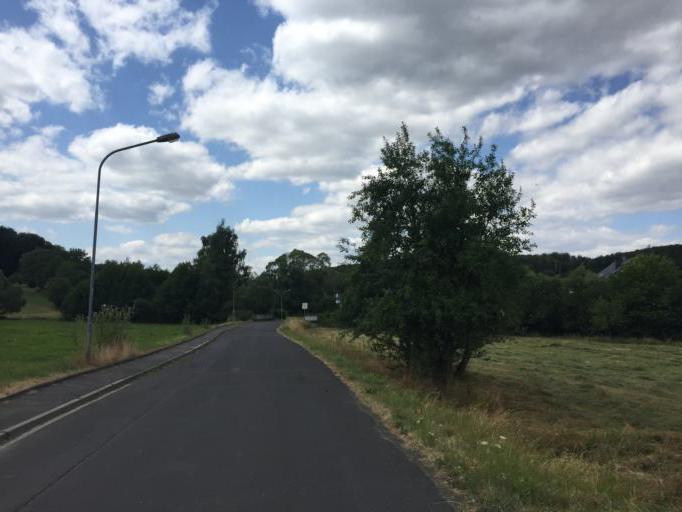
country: DE
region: Hesse
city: Lollar
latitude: 50.6450
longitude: 8.6758
